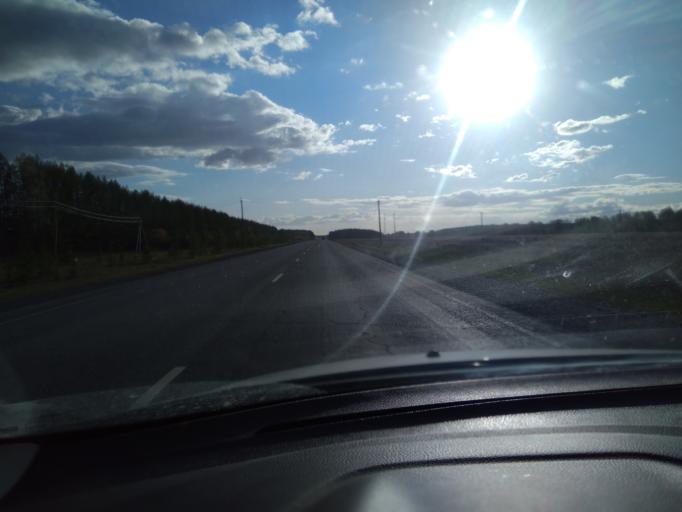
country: RU
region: Sverdlovsk
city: Troitskiy
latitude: 57.0897
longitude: 63.7740
